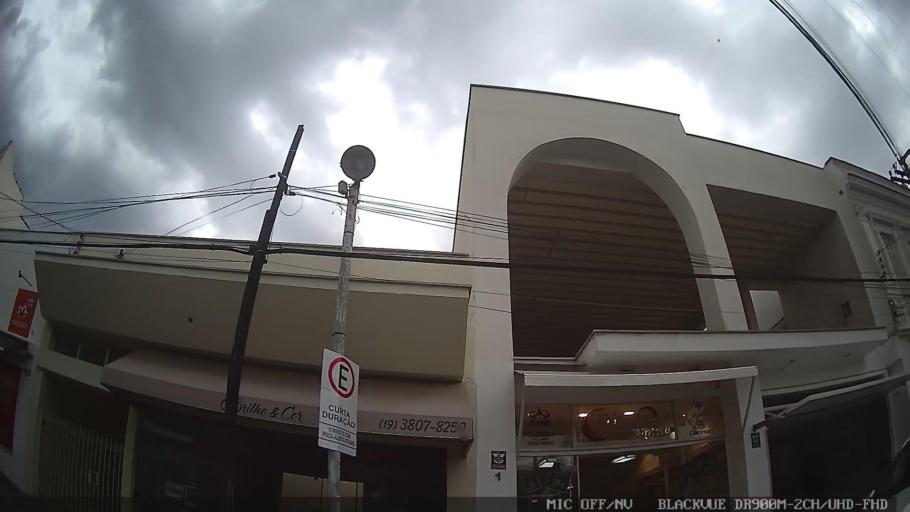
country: BR
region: Sao Paulo
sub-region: Amparo
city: Amparo
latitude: -22.7044
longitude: -46.7682
